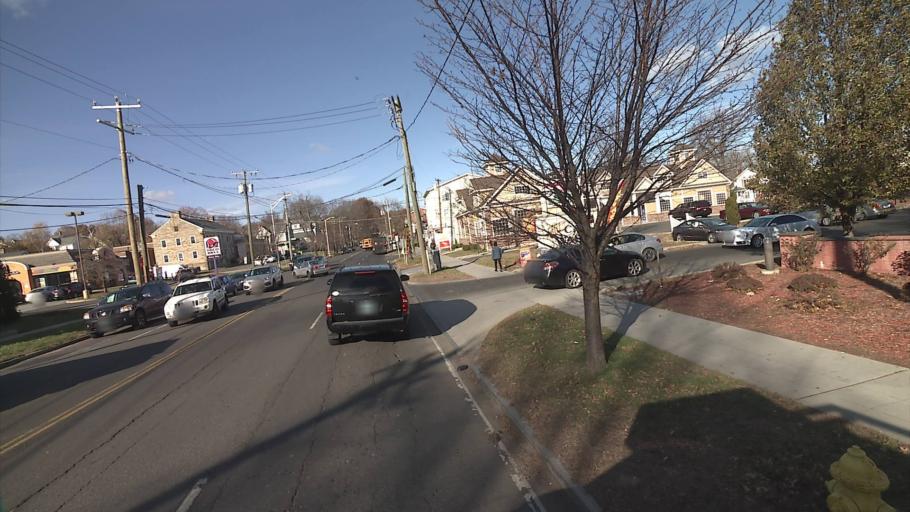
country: US
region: Connecticut
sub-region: Fairfield County
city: Danbury
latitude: 41.4016
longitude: -73.4588
